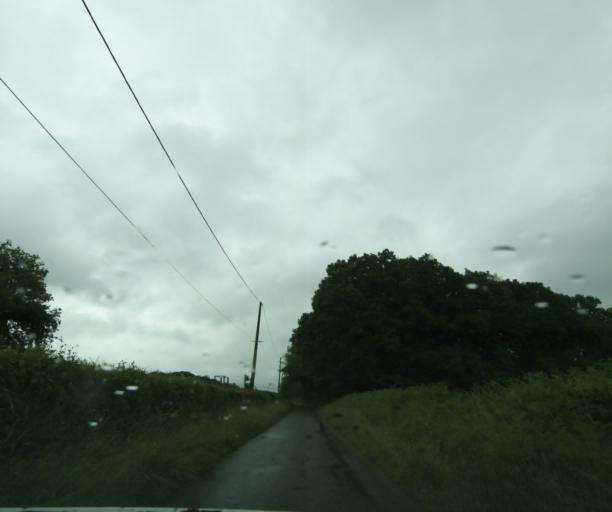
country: FR
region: Bourgogne
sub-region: Departement de Saone-et-Loire
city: Charolles
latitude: 46.5116
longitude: 4.2867
